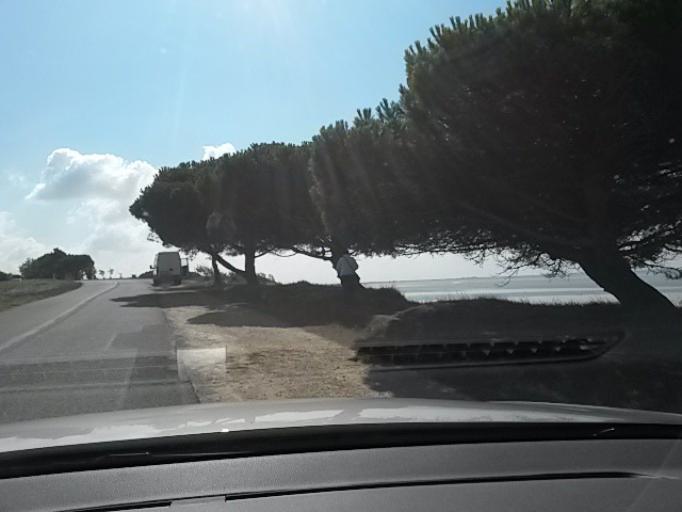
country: FR
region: Poitou-Charentes
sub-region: Departement de la Charente-Maritime
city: Port-des-Barques
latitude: 45.9431
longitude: -1.0975
